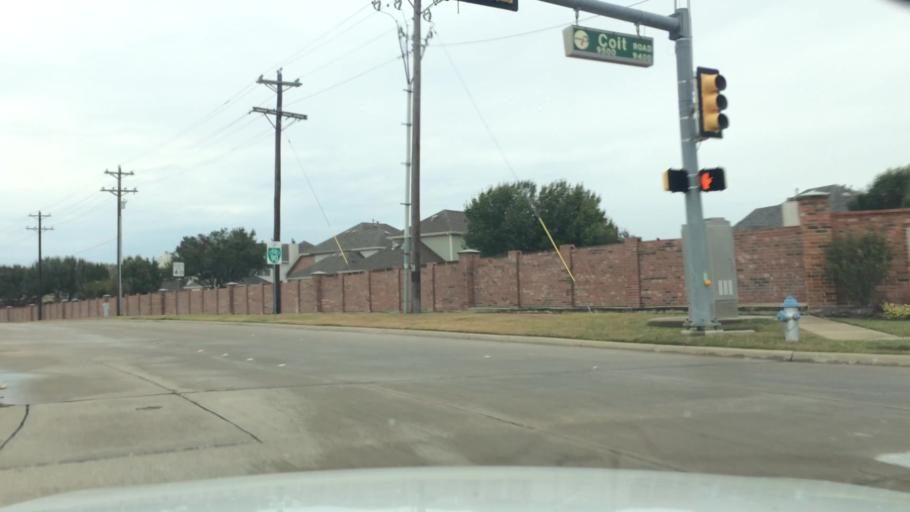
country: US
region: Texas
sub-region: Collin County
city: Frisco
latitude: 33.1071
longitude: -96.7681
